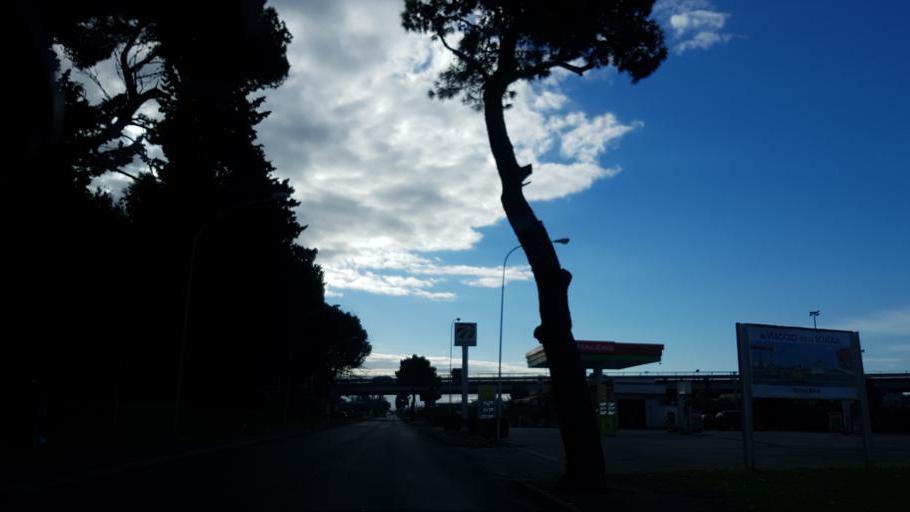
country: IT
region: Apulia
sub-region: Provincia di Brindisi
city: Brindisi
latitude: 40.6275
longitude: 17.9473
